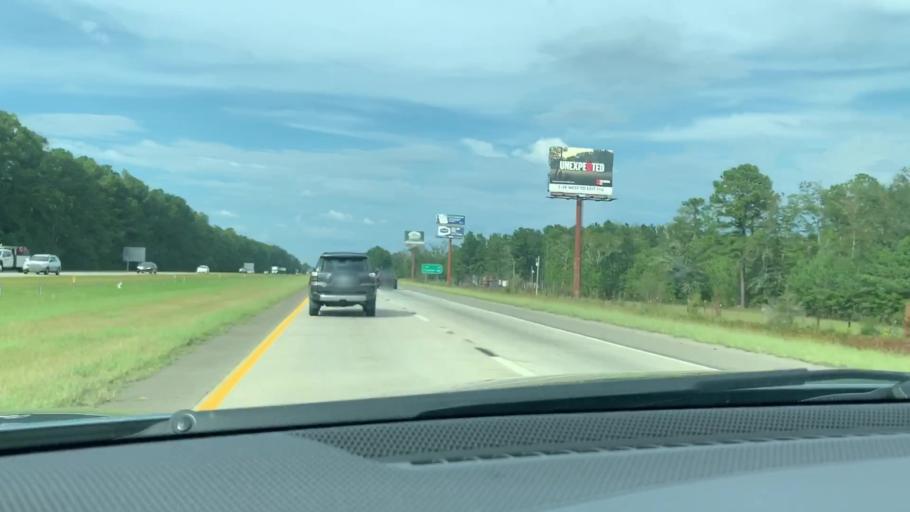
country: US
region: South Carolina
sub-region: Colleton County
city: Walterboro
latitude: 32.9426
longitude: -80.6846
